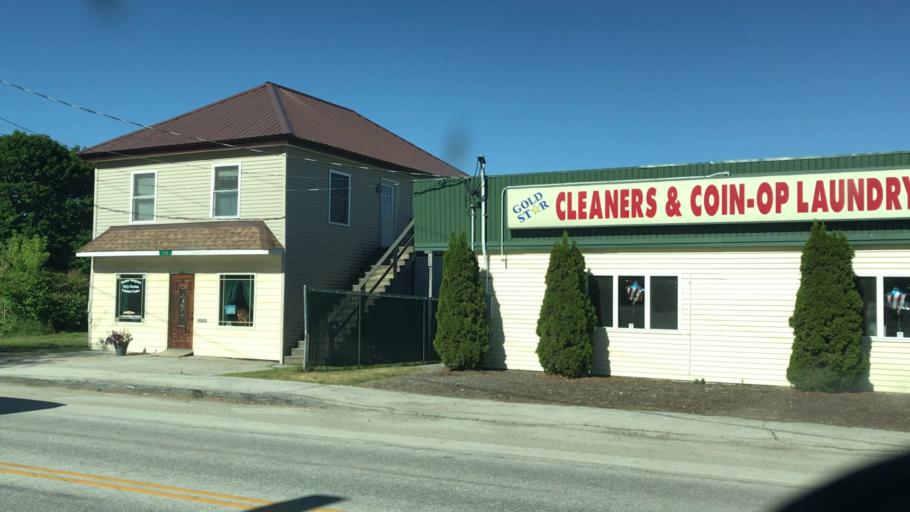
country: US
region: Maine
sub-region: Penobscot County
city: Lincoln
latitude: 45.3675
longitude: -68.5030
